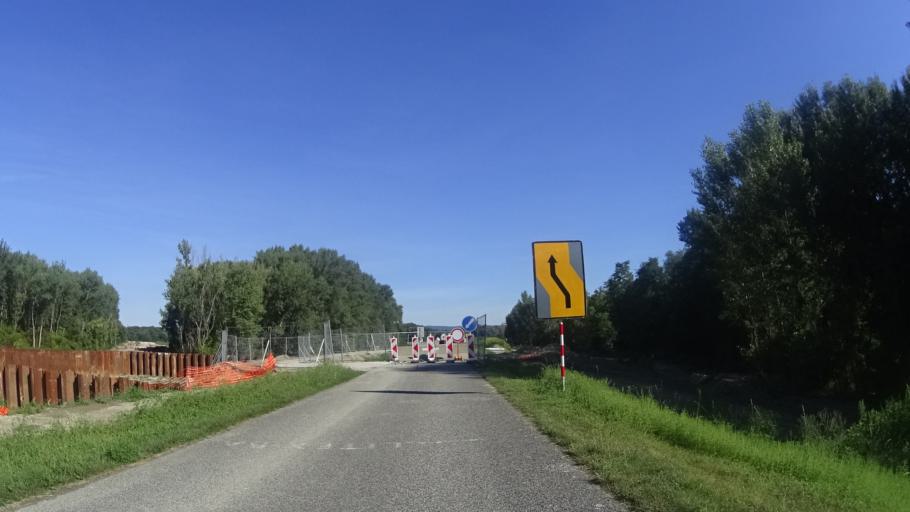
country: SK
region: Bratislavsky
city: Bratislava
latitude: 48.1025
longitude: 17.1477
